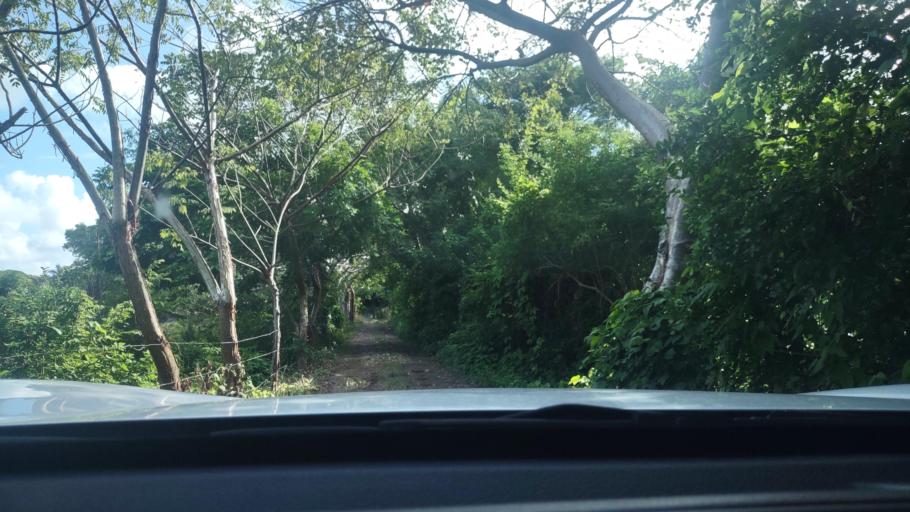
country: MX
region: Veracruz
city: El Tejar
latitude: 19.0800
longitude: -96.1663
